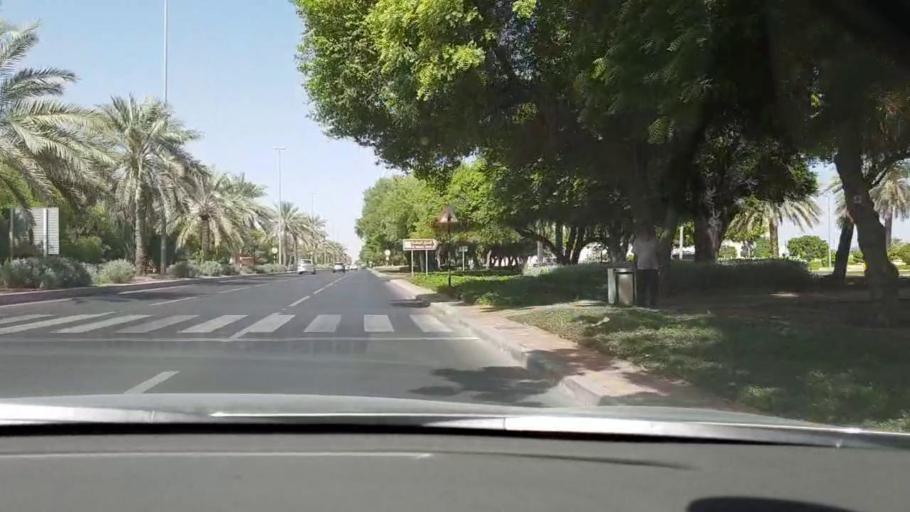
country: OM
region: Al Buraimi
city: Al Buraymi
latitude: 24.2424
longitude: 55.7392
